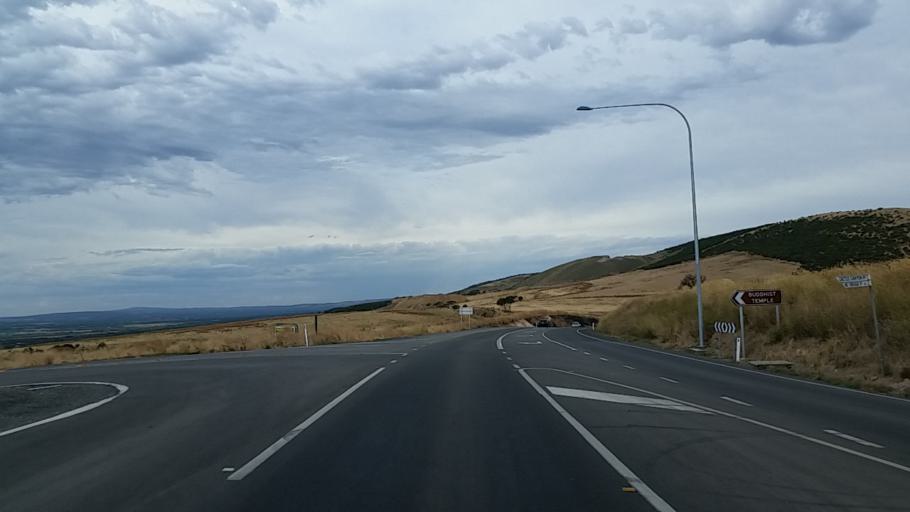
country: AU
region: South Australia
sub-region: Onkaparinga
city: Port Willunga
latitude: -35.3512
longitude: 138.4495
